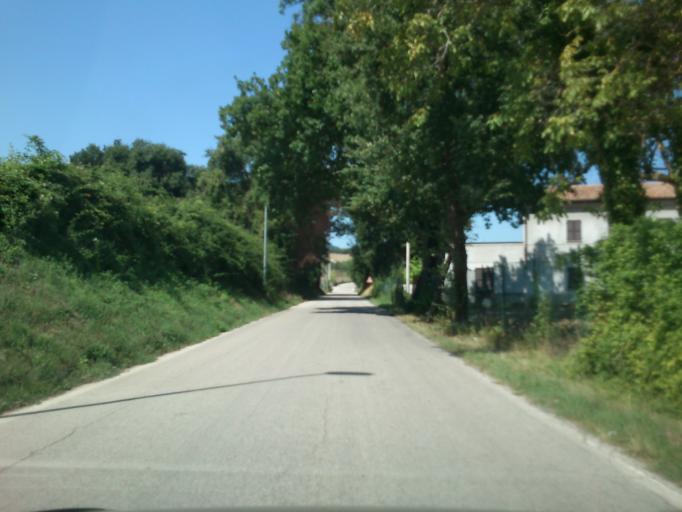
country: IT
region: The Marches
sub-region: Provincia di Pesaro e Urbino
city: Calcinelli
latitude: 43.7763
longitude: 12.9080
